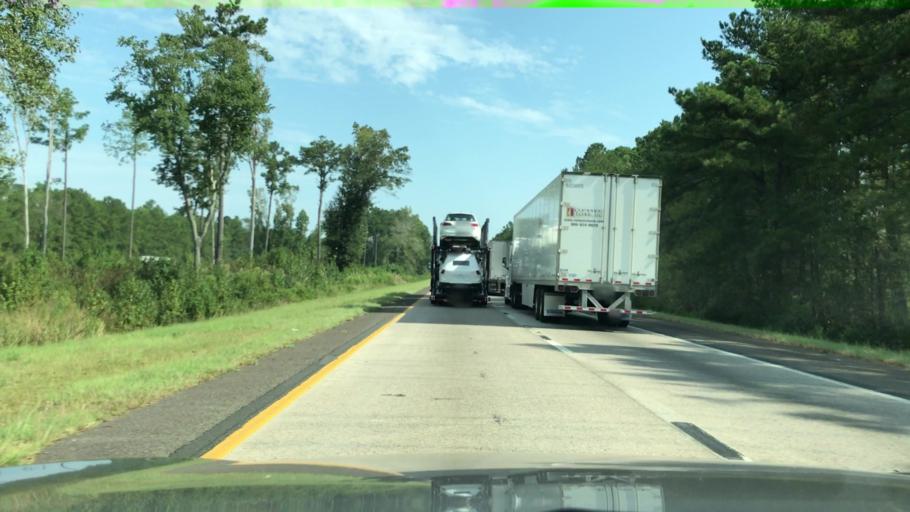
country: US
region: South Carolina
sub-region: Colleton County
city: Walterboro
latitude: 32.8604
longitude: -80.7274
